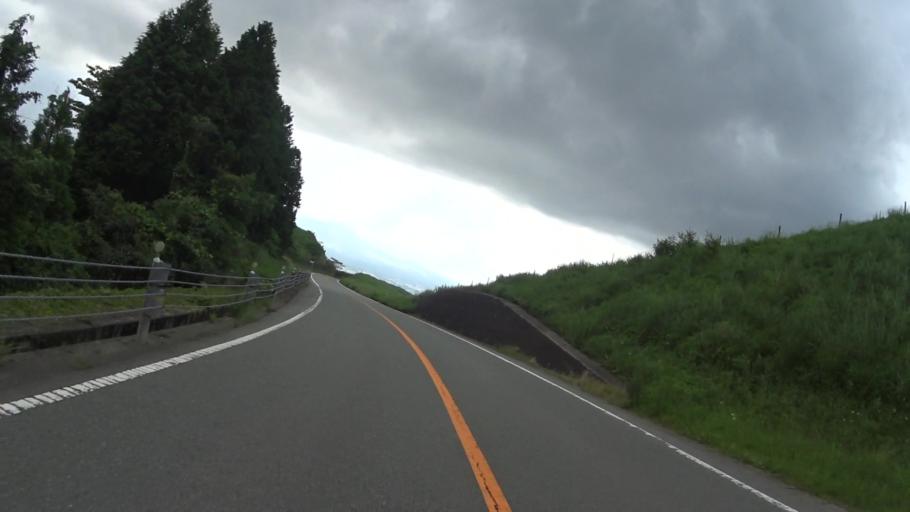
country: JP
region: Kumamoto
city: Aso
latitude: 32.9801
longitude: 131.1445
